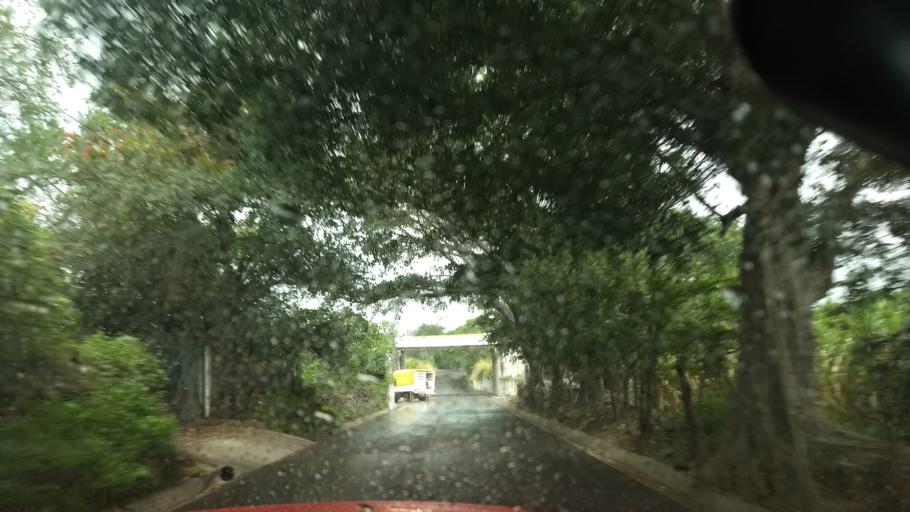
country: MX
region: Jalisco
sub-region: Tonila
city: San Marcos
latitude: 19.4410
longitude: -103.4920
